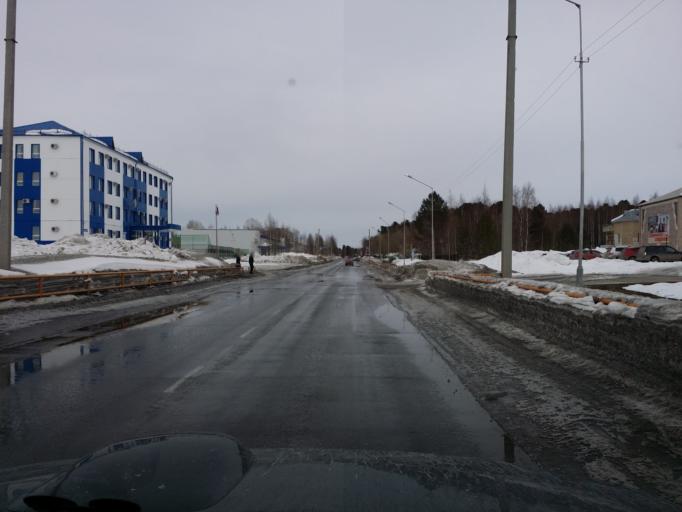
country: RU
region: Tomsk
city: Strezhevoy
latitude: 60.7257
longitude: 77.5969
